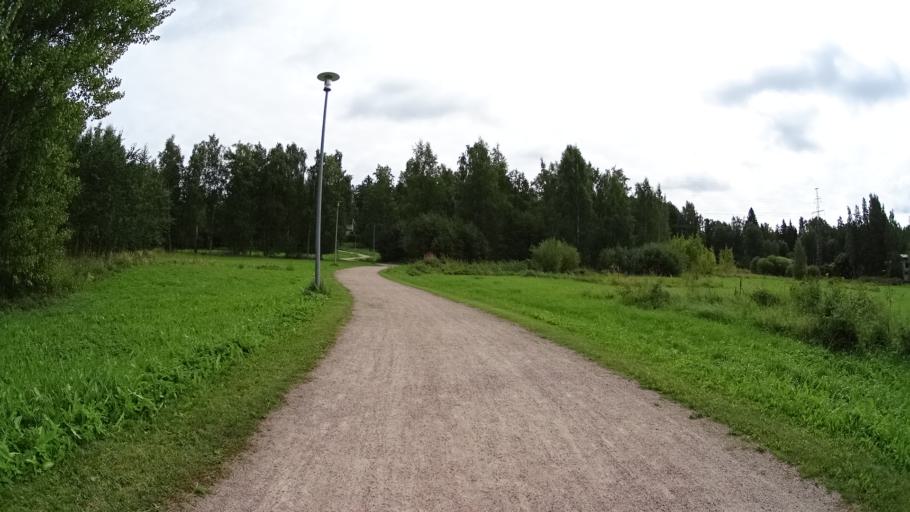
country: FI
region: Uusimaa
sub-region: Helsinki
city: Teekkarikylae
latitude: 60.2675
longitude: 24.8891
